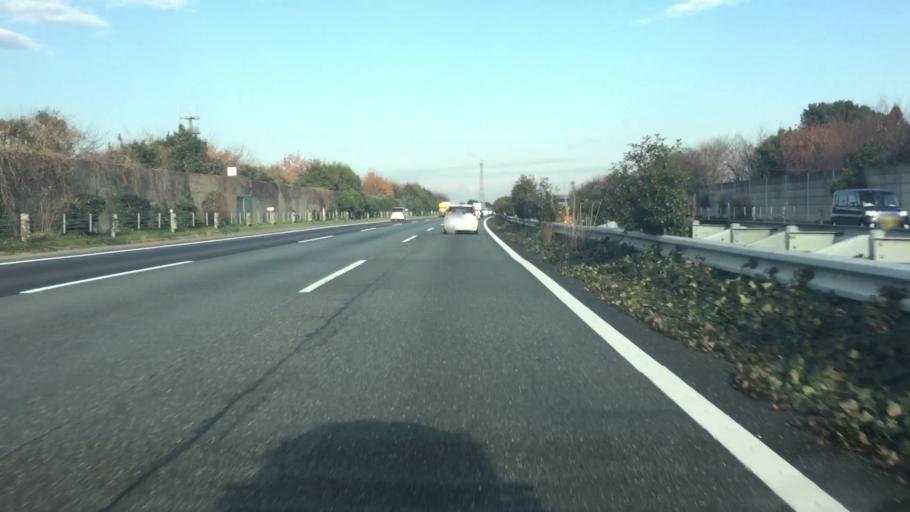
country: JP
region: Saitama
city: Yorii
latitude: 36.1385
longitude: 139.2271
